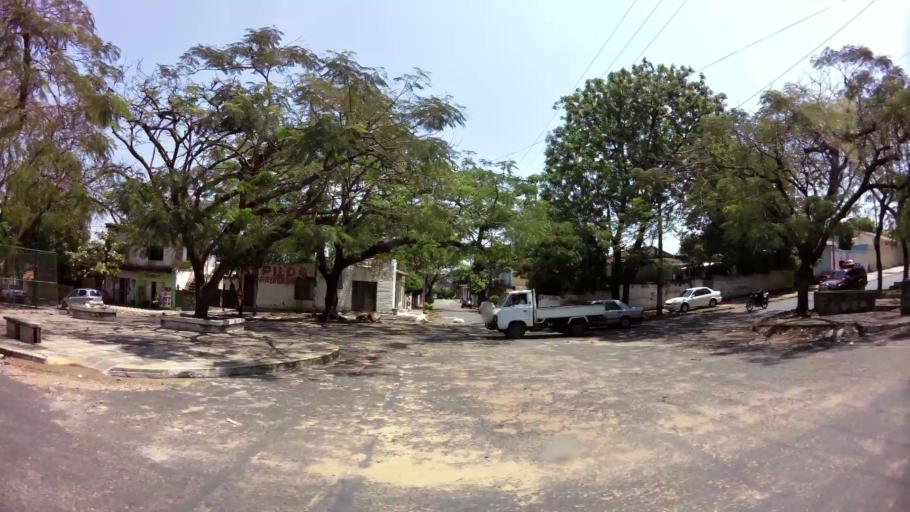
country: PY
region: Asuncion
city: Asuncion
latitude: -25.3057
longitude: -57.6391
